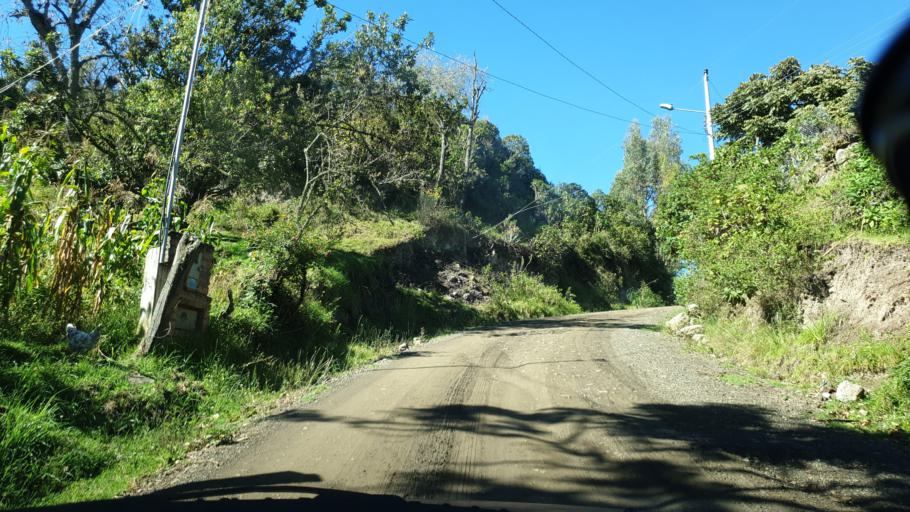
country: EC
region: Azuay
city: Llacao
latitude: -2.8745
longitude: -78.9044
